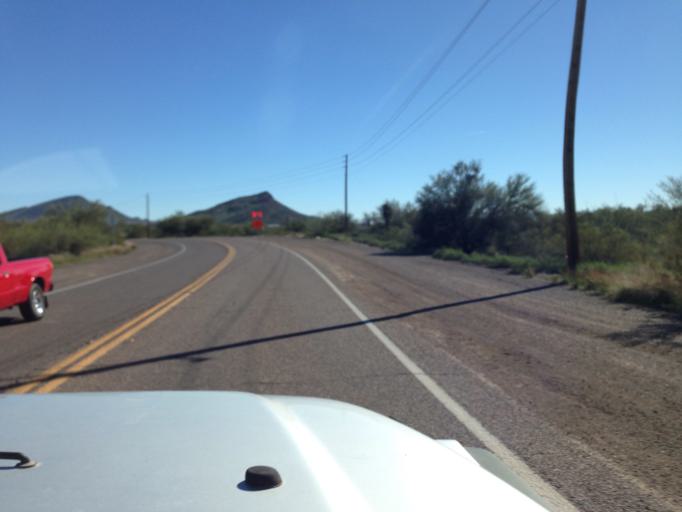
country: US
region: Arizona
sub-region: Maricopa County
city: New River
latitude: 33.9027
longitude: -112.0819
